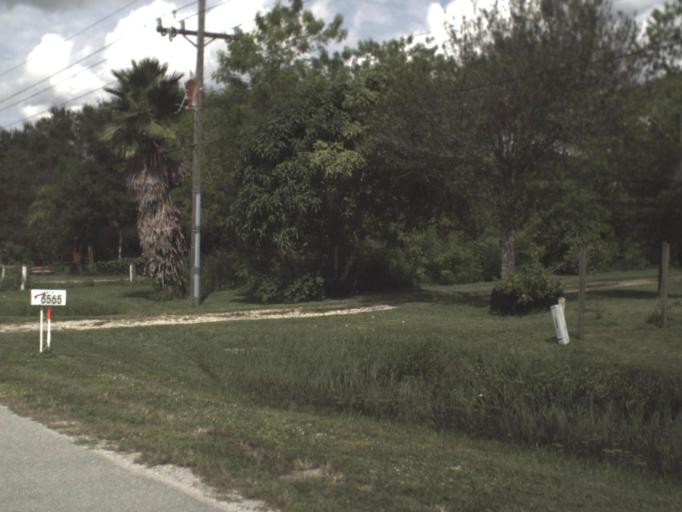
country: US
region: Florida
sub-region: Hendry County
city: Port LaBelle
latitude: 26.6671
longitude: -81.4363
